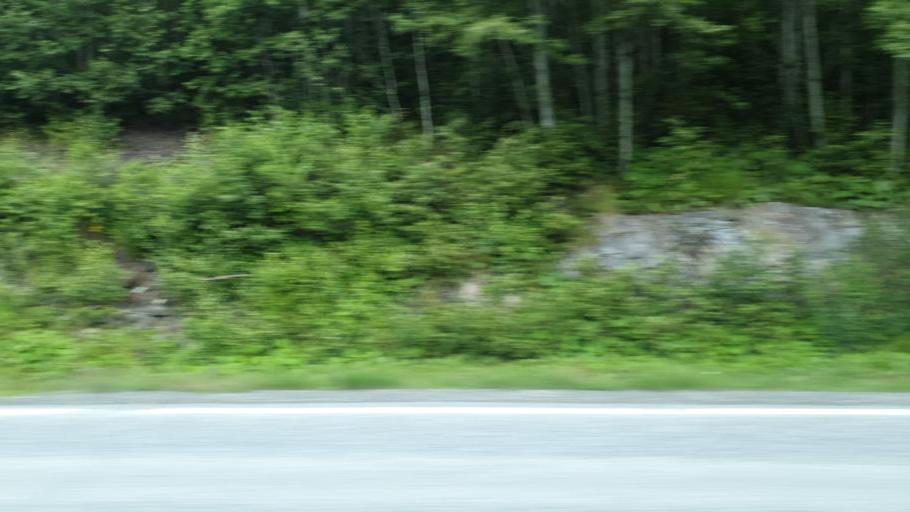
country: NO
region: Sor-Trondelag
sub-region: Midtre Gauldal
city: Storen
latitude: 63.0120
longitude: 10.2461
